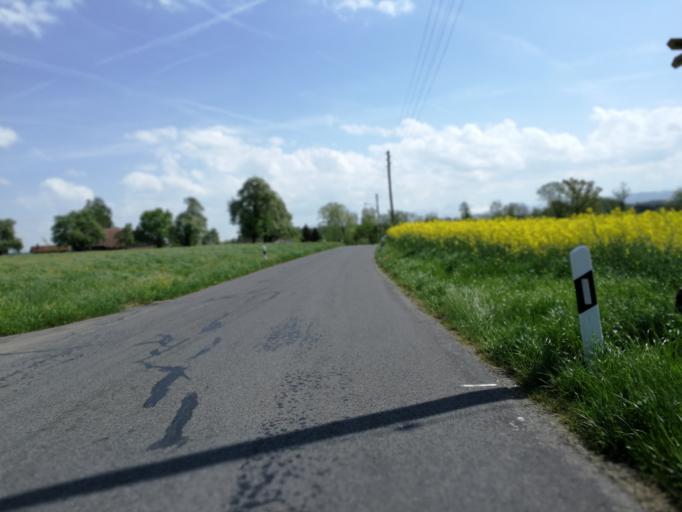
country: CH
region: Zurich
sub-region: Bezirk Hinwil
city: Gossau
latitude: 47.2951
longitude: 8.7706
